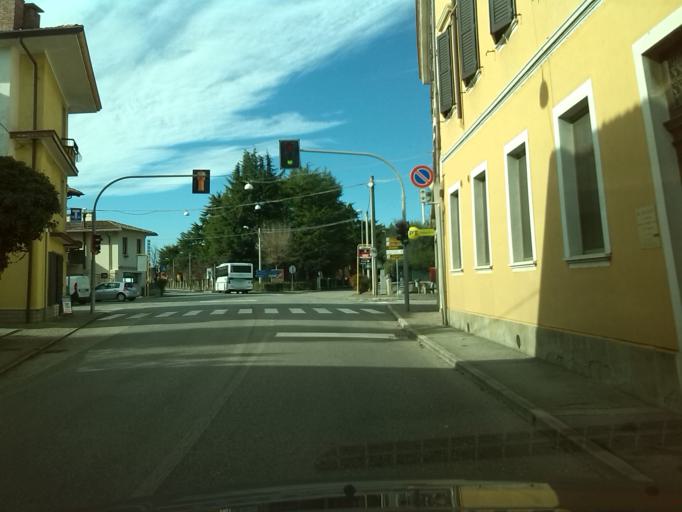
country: IT
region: Friuli Venezia Giulia
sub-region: Provincia di Udine
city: Corno di Rosazzo
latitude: 45.9737
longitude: 13.4555
